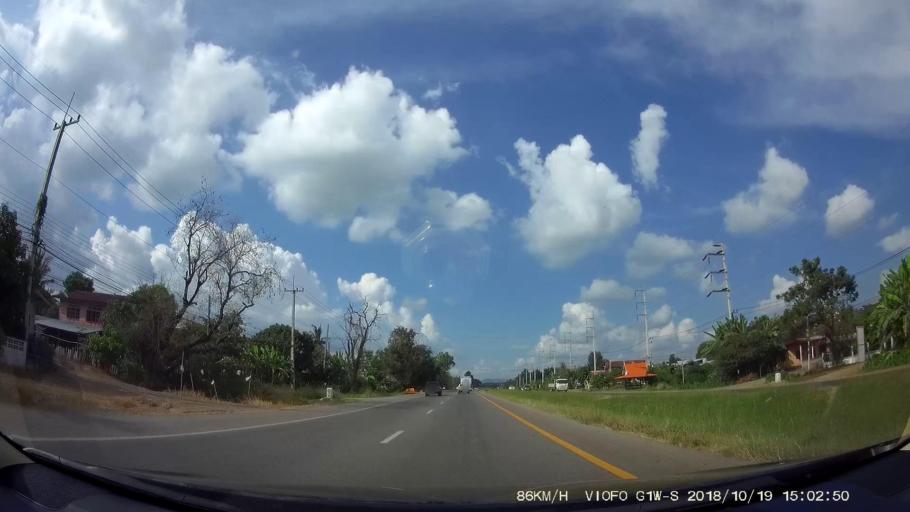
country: TH
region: Chaiyaphum
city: Phu Khiao
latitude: 16.4038
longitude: 102.1313
